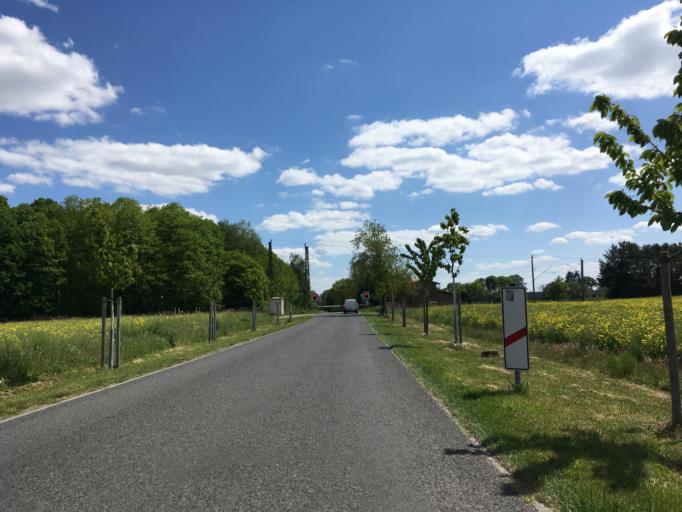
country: DE
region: Brandenburg
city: Biesenthal
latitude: 52.7397
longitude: 13.6572
